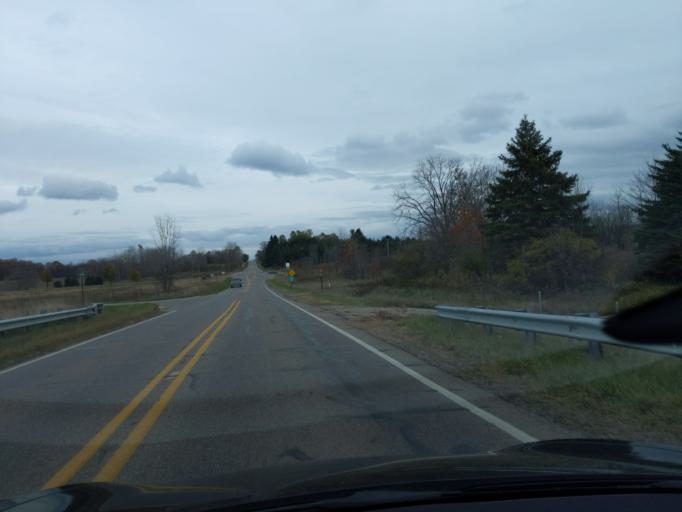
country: US
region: Michigan
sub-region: Ingham County
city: East Lansing
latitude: 42.7841
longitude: -84.5116
